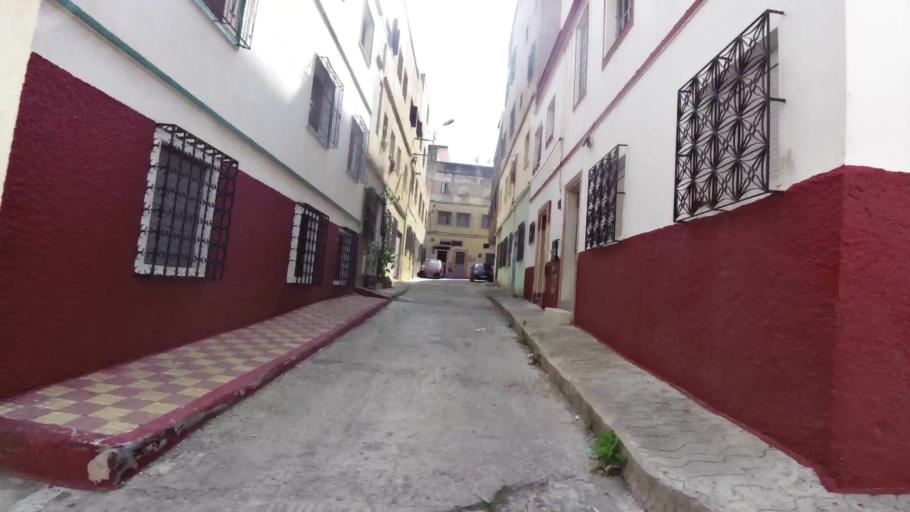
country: MA
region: Tanger-Tetouan
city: Tetouan
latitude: 35.5816
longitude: -5.3596
